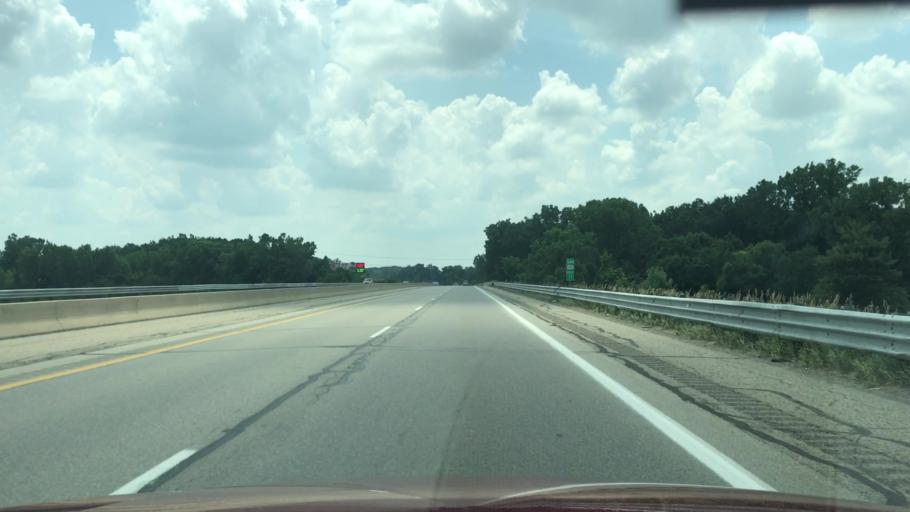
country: US
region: Michigan
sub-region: Kent County
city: Byron Center
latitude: 42.7669
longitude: -85.6723
